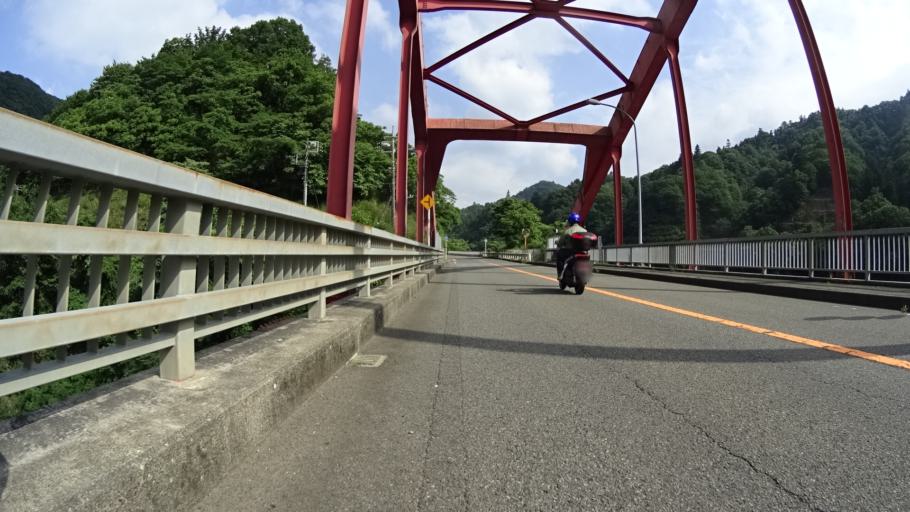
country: JP
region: Kanagawa
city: Atsugi
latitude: 35.5095
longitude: 139.2505
